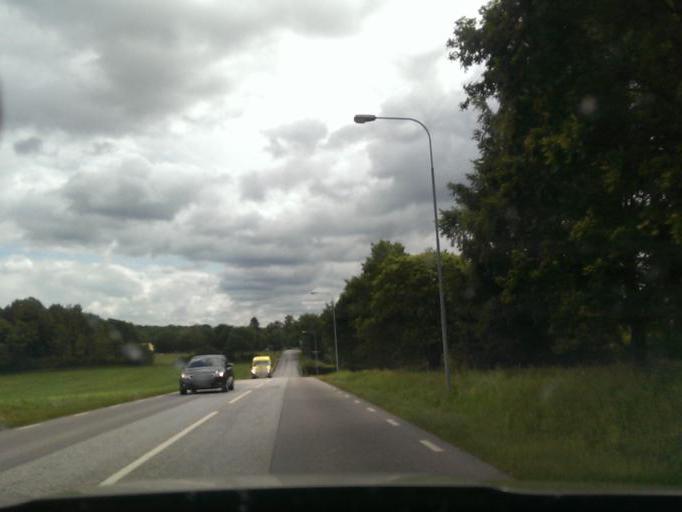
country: SE
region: Skane
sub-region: Eslovs Kommun
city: Stehag
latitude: 55.9458
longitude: 13.3662
